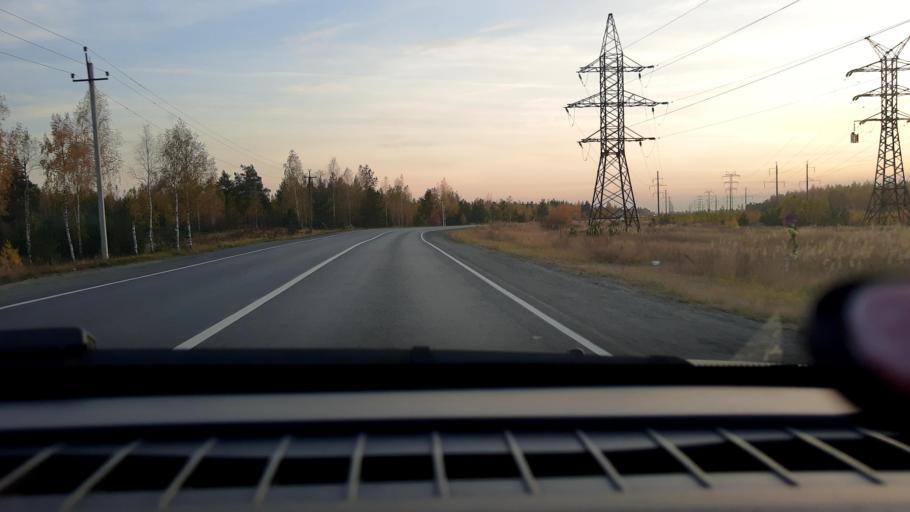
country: RU
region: Nizjnij Novgorod
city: Lukino
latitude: 56.3381
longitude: 43.5782
